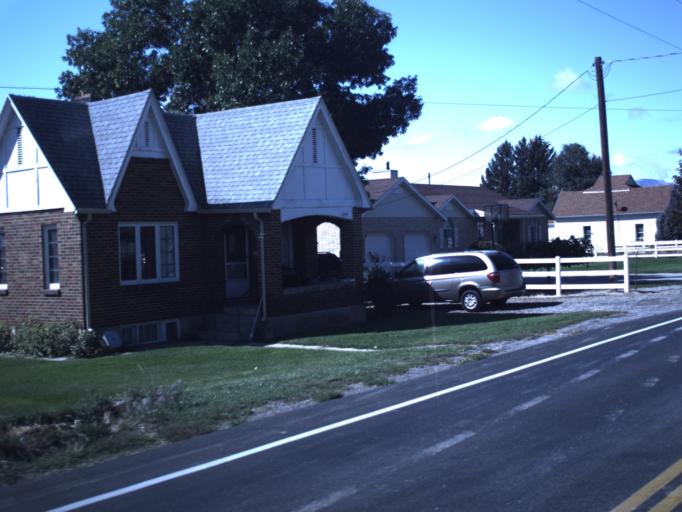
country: US
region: Utah
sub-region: Utah County
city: Spanish Fork
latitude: 40.0984
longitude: -111.6846
